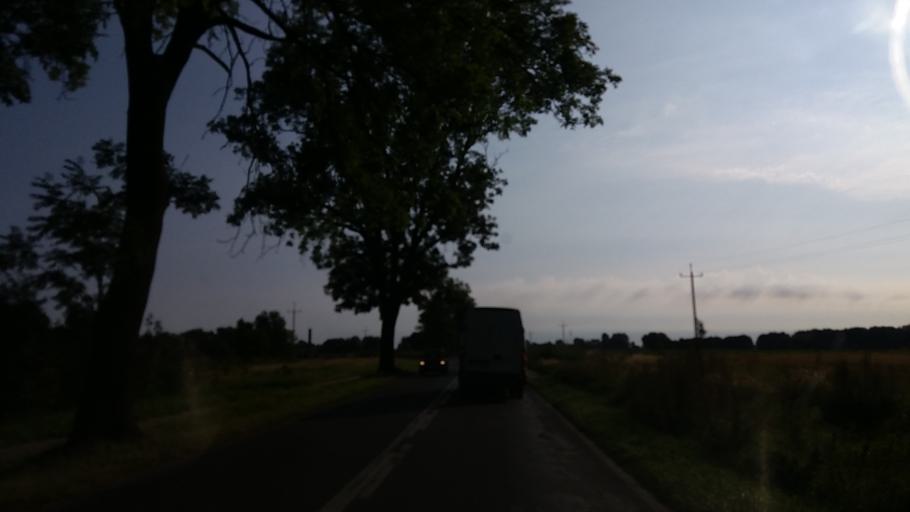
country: PL
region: West Pomeranian Voivodeship
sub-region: Powiat choszczenski
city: Choszczno
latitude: 53.1675
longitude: 15.4538
